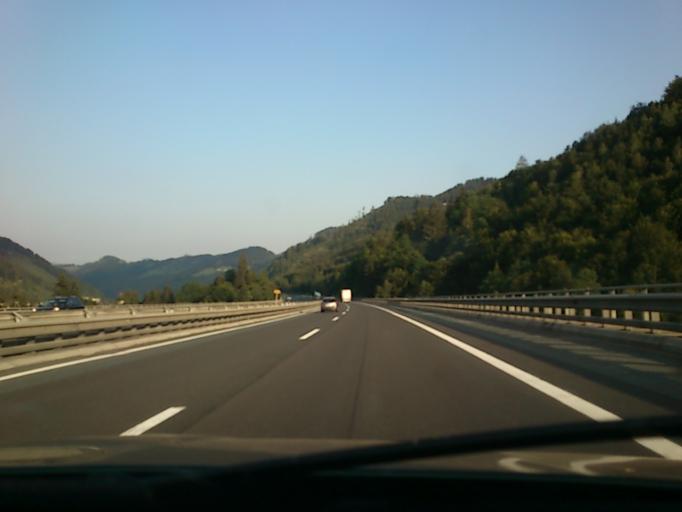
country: AT
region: Styria
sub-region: Politischer Bezirk Graz-Umgebung
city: Ubelbach
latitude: 47.2309
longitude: 15.2155
